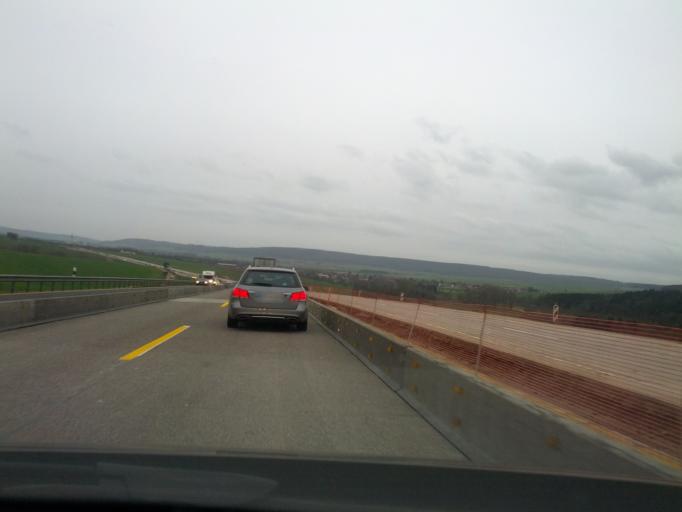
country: DE
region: Lower Saxony
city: Bockenem
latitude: 51.9658
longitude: 10.1424
